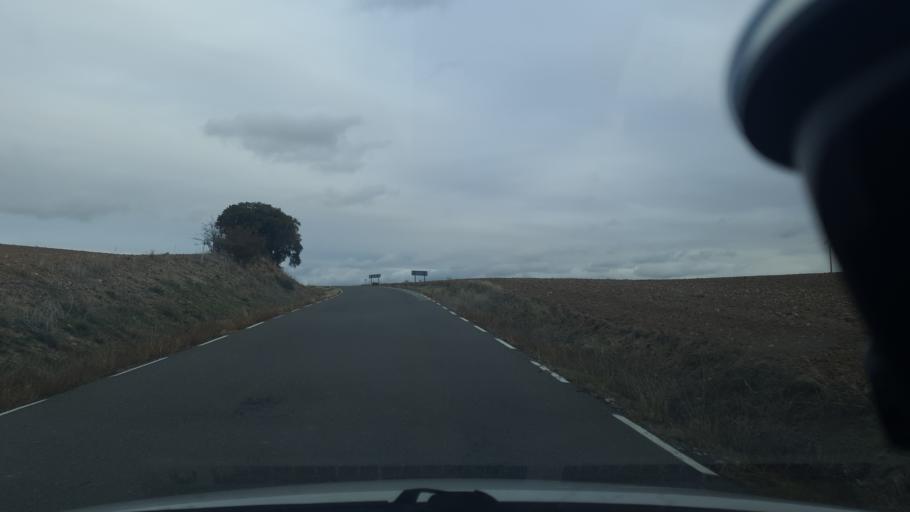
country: ES
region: Castille and Leon
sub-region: Provincia de Avila
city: Gotarrendura
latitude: 40.8267
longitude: -4.7135
